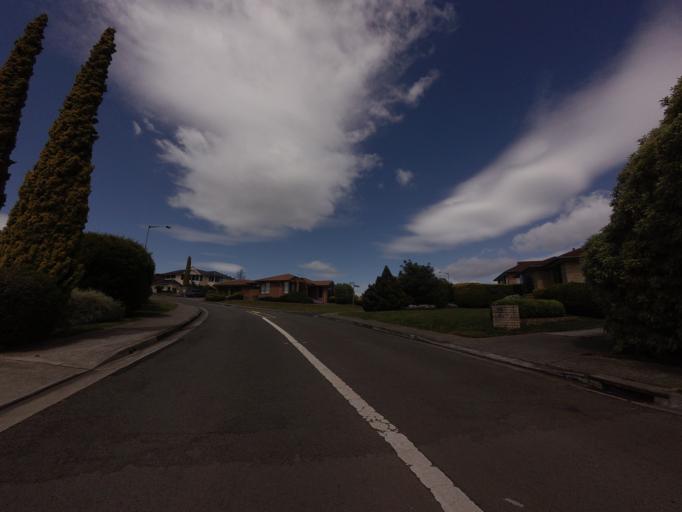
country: AU
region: Tasmania
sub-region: Clarence
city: Howrah
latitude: -42.8853
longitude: 147.4092
